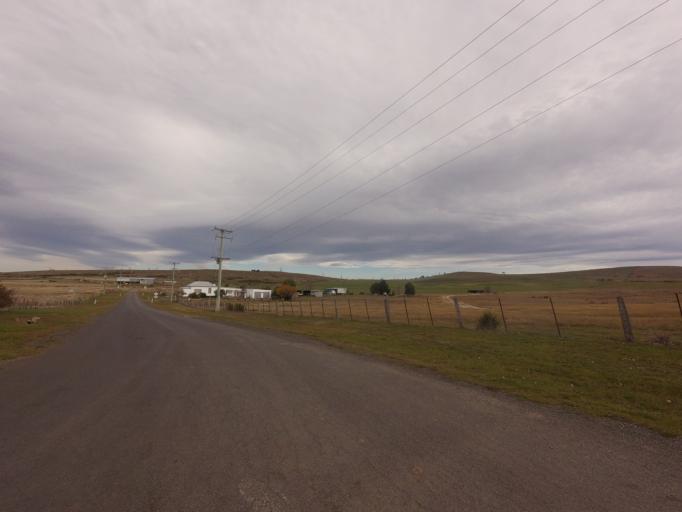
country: AU
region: Tasmania
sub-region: Derwent Valley
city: New Norfolk
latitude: -42.3835
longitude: 146.9858
